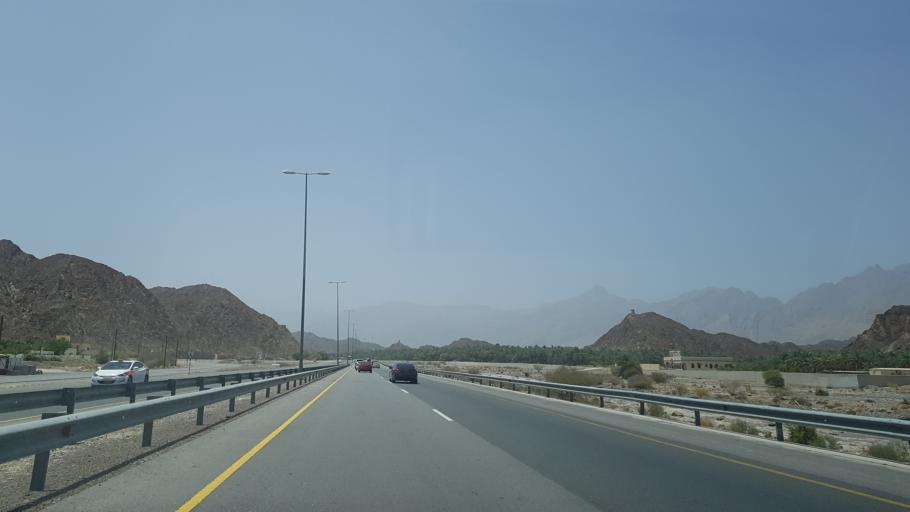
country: OM
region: Muhafazat ad Dakhiliyah
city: Sufalat Sama'il
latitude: 23.3555
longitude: 58.0282
